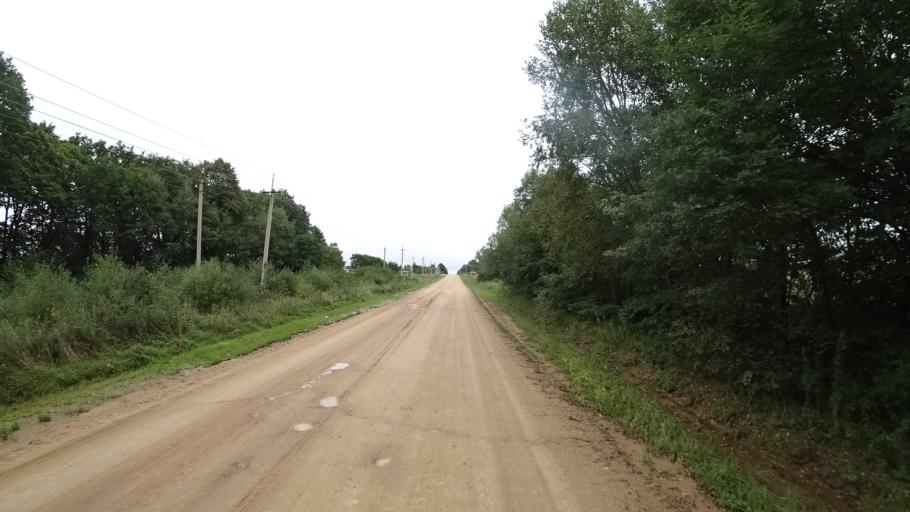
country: RU
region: Primorskiy
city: Monastyrishche
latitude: 44.0756
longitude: 132.5866
